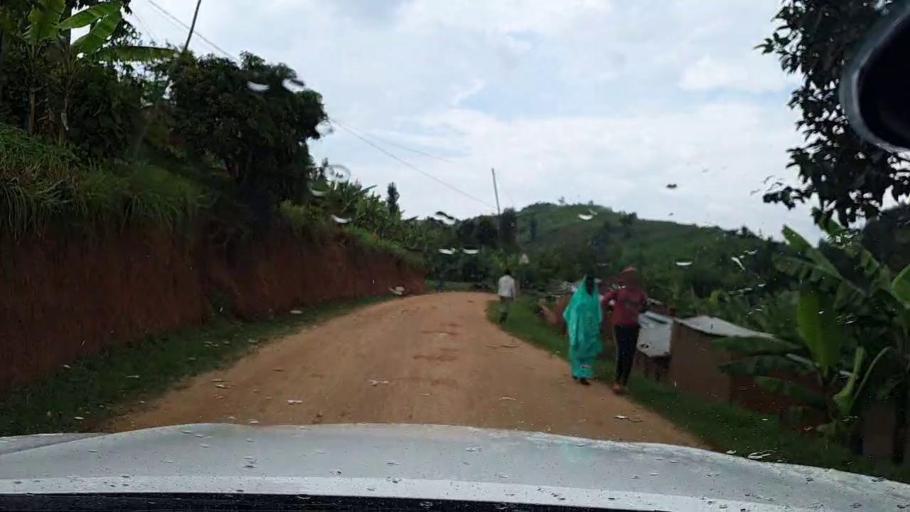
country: RW
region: Western Province
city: Kibuye
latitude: -2.1151
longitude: 29.4205
